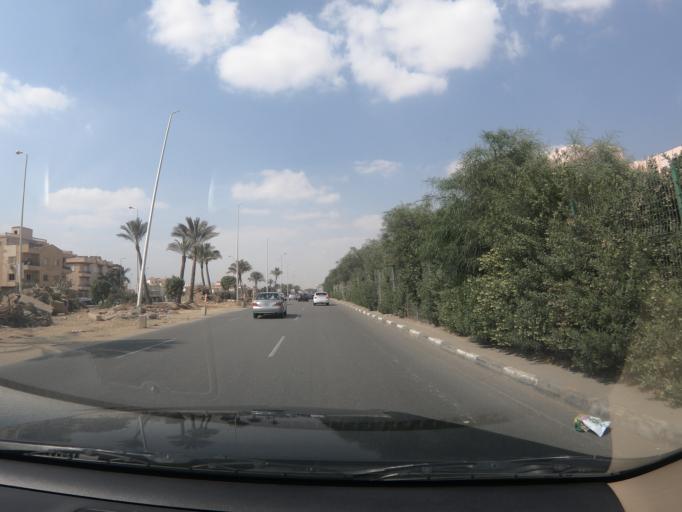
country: EG
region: Muhafazat al Qalyubiyah
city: Al Khankah
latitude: 30.0623
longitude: 31.4752
